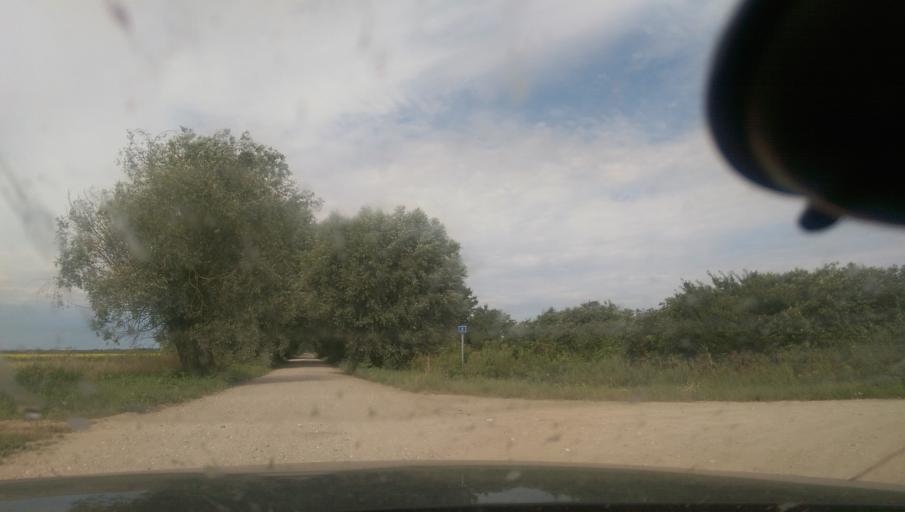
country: LT
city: Rusne
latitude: 55.2933
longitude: 21.3564
